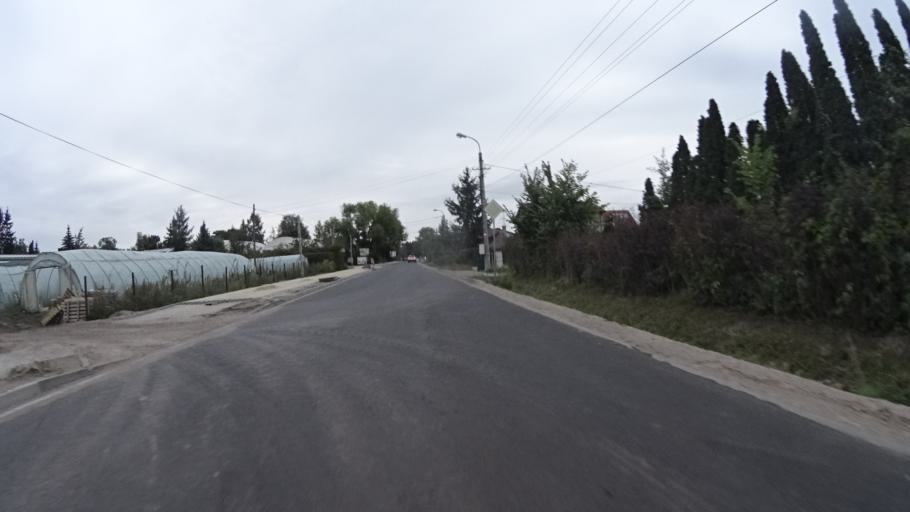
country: PL
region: Masovian Voivodeship
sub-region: Powiat warszawski zachodni
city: Stare Babice
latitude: 52.2675
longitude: 20.8293
